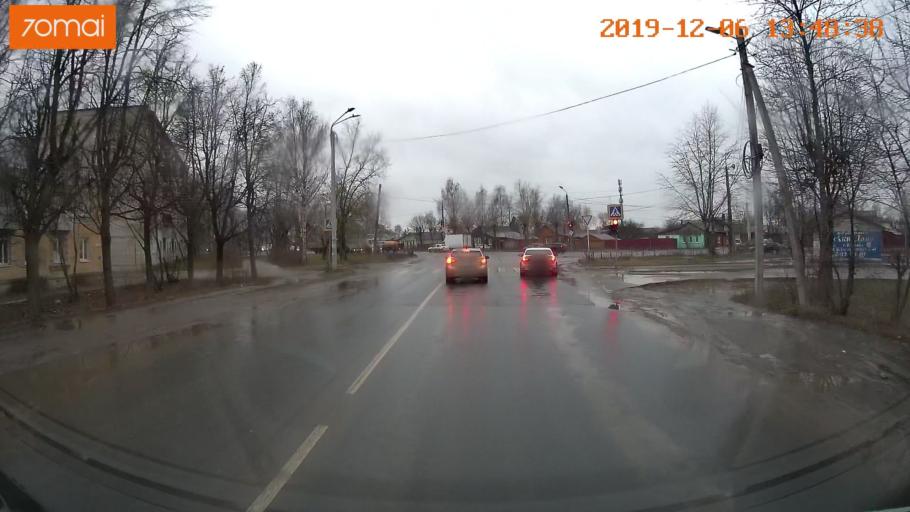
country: RU
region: Ivanovo
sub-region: Gorod Ivanovo
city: Ivanovo
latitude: 56.9809
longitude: 40.9546
